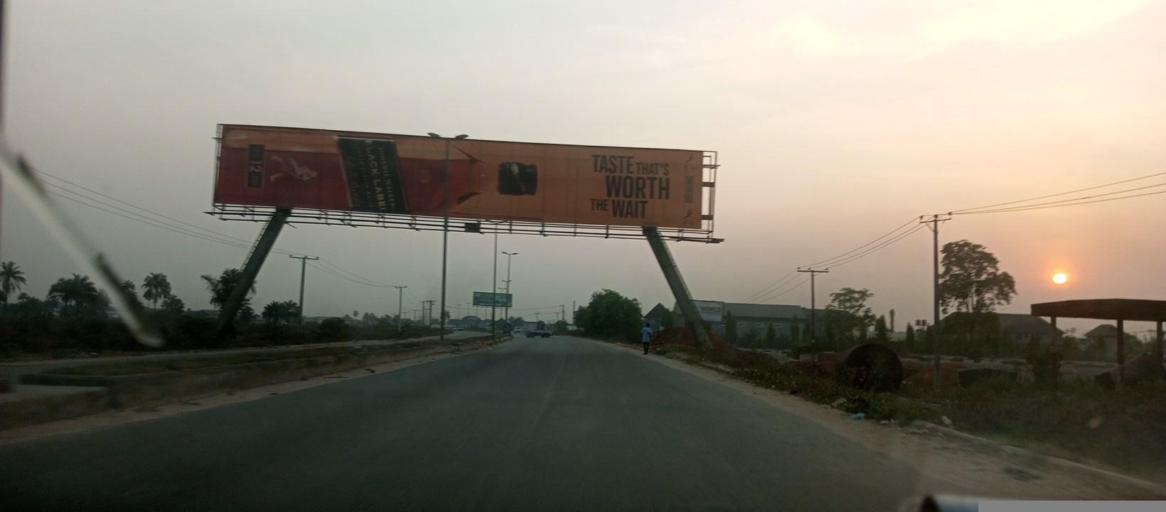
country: NG
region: Rivers
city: Emuoha
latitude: 4.9288
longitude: 7.0004
